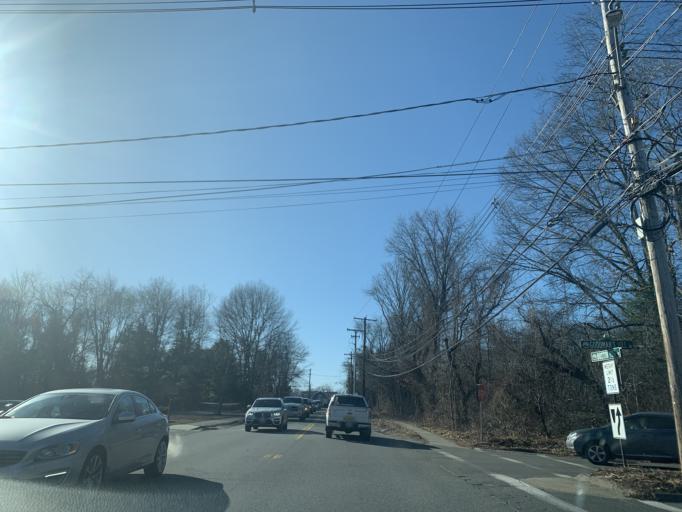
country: US
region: Massachusetts
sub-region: Middlesex County
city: Sudbury
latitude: 42.3627
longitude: -71.3971
